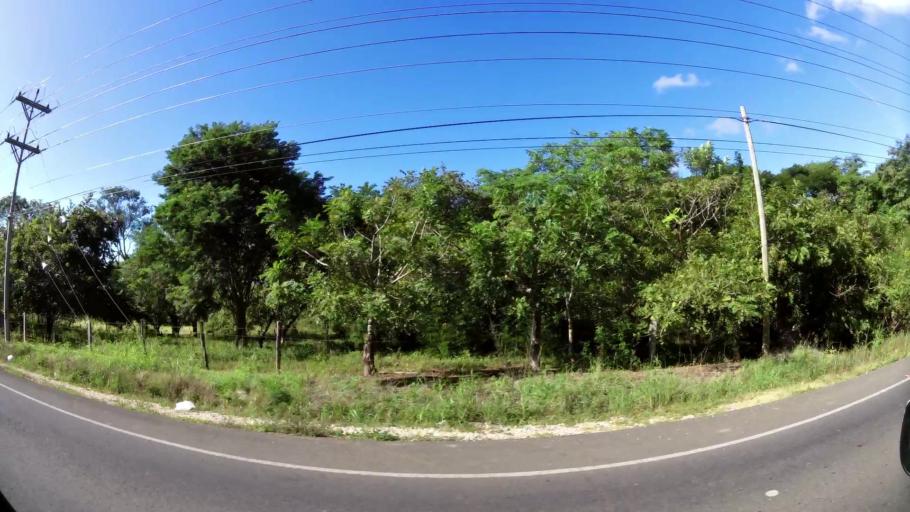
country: CR
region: Guanacaste
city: Sardinal
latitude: 10.3798
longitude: -85.7867
